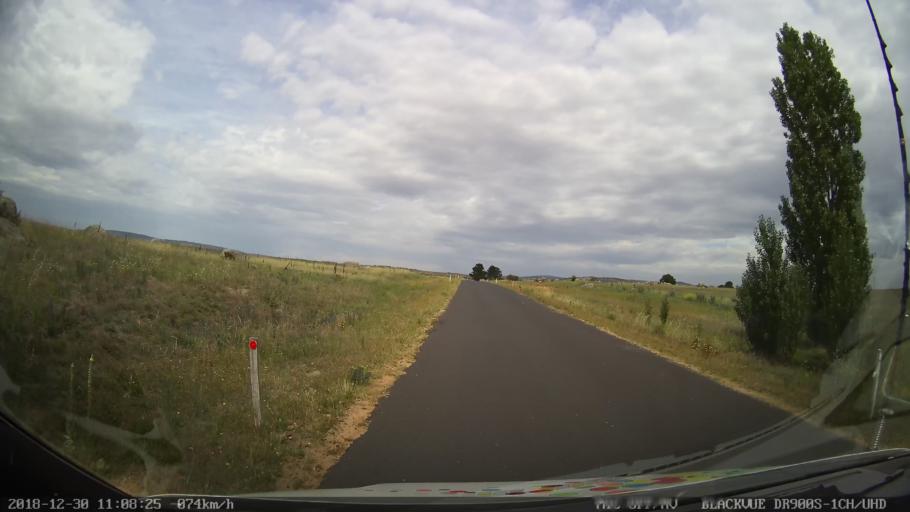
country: AU
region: New South Wales
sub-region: Snowy River
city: Berridale
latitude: -36.5031
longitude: 148.8070
